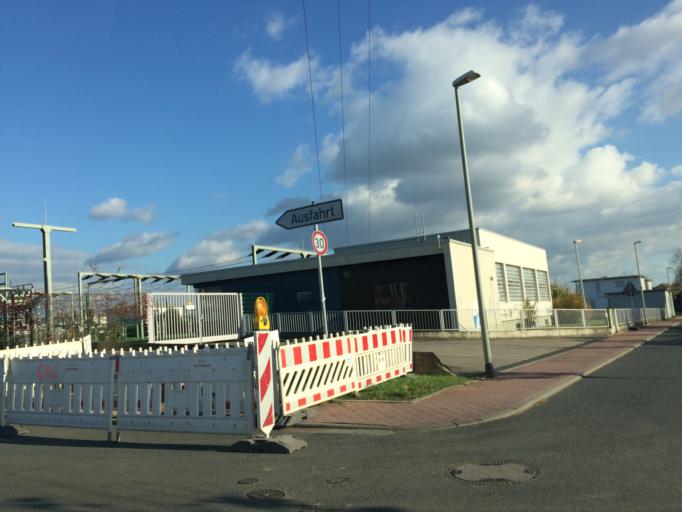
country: DE
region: Hesse
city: Liederbach
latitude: 50.1335
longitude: 8.4907
